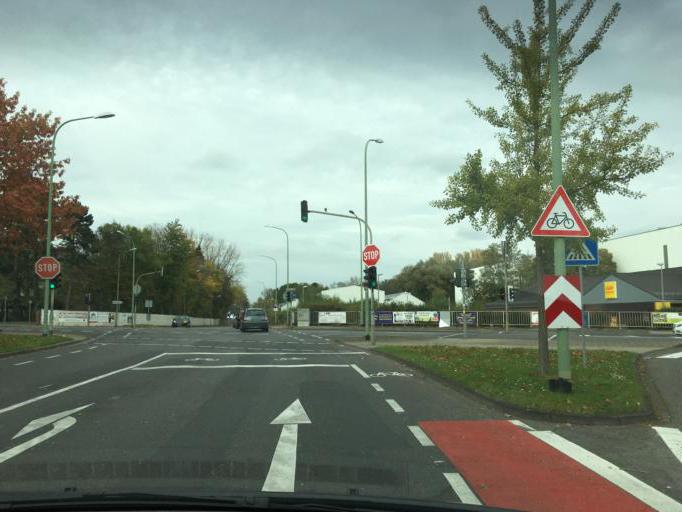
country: DE
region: North Rhine-Westphalia
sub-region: Regierungsbezirk Koln
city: Dueren
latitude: 50.7965
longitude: 6.4626
